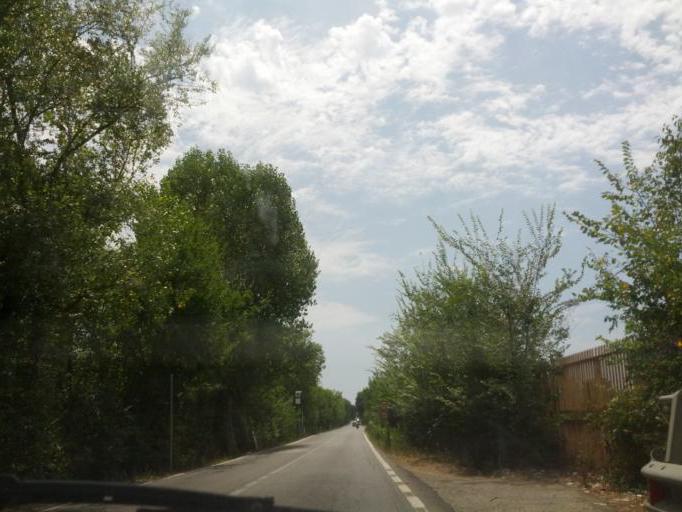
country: IT
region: Latium
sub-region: Provincia di Latina
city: Fondi
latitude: 41.3102
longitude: 13.4003
